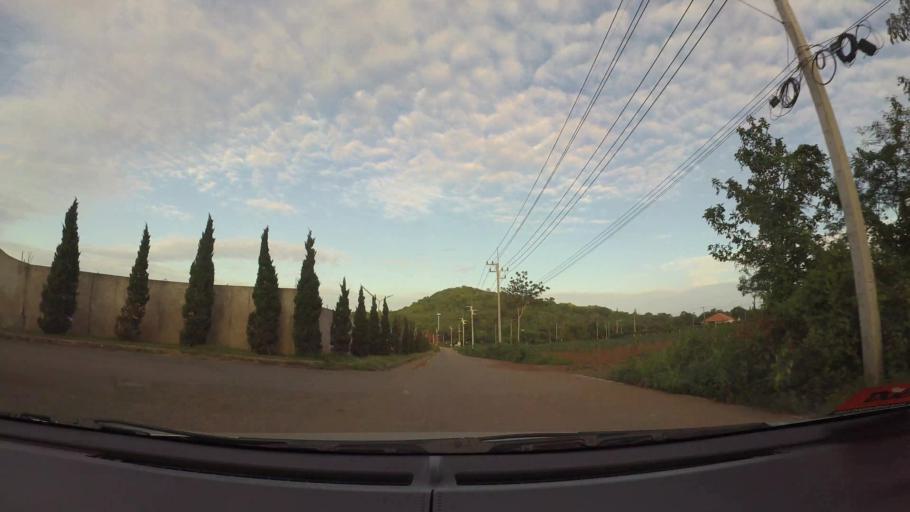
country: TH
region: Chon Buri
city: Sattahip
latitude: 12.7524
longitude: 100.9517
